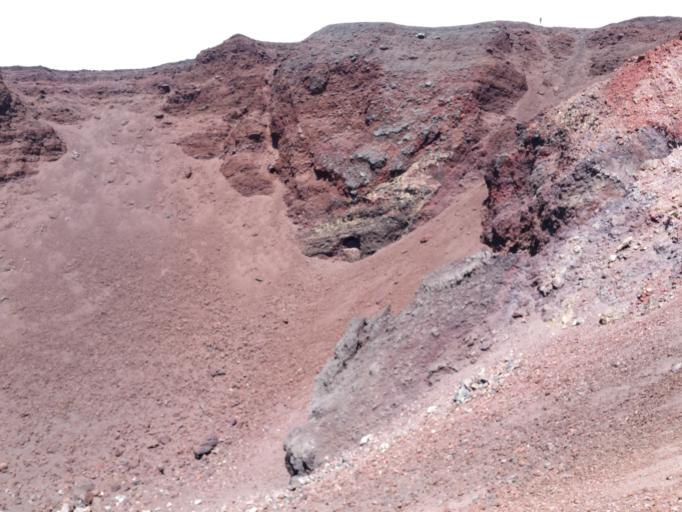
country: IT
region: Sicily
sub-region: Catania
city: Nicolosi
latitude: 37.7220
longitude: 15.0042
